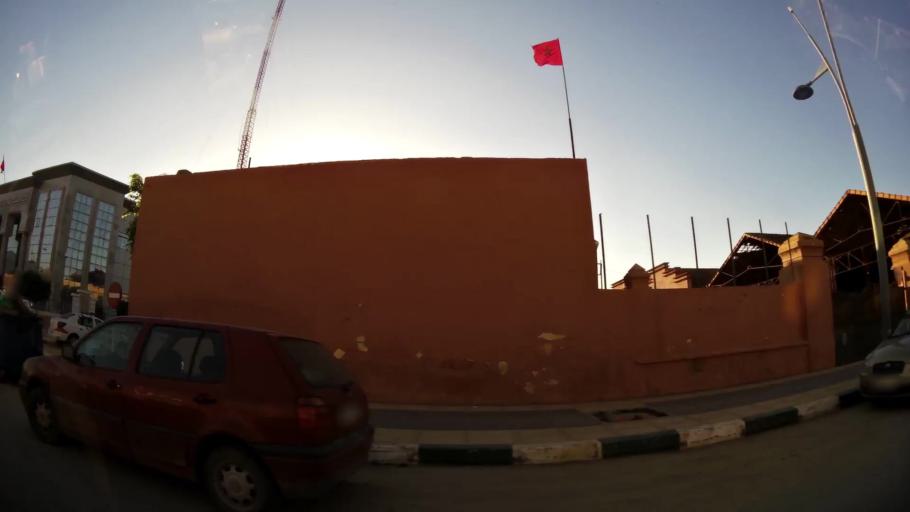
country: MA
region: Oriental
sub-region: Berkane-Taourirt
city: Berkane
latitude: 34.9315
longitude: -2.3272
